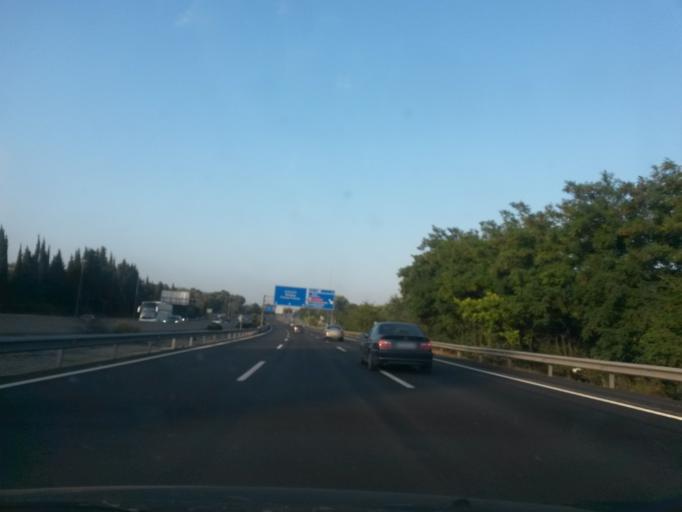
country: ES
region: Catalonia
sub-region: Provincia de Barcelona
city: Sant Cugat del Valles
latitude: 41.4888
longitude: 2.0862
